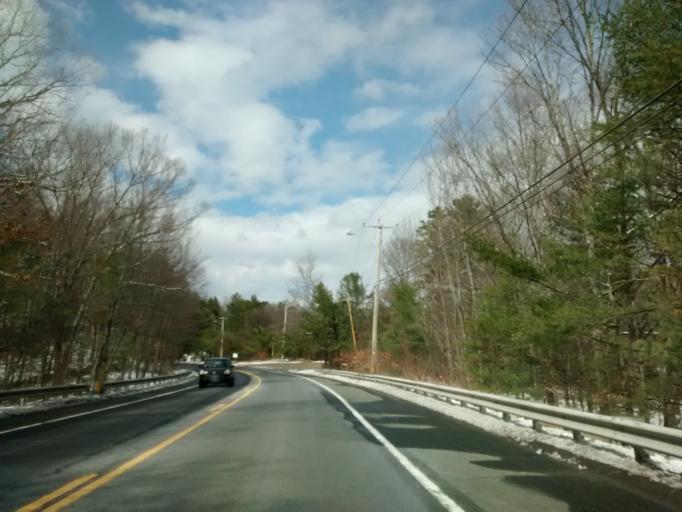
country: US
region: Massachusetts
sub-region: Worcester County
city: Whitinsville
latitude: 42.1140
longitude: -71.6375
